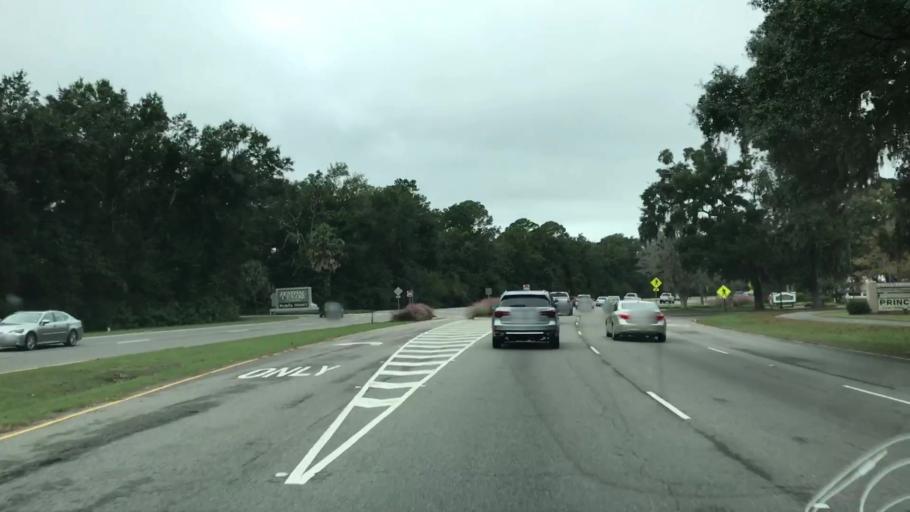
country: US
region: South Carolina
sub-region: Beaufort County
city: Hilton Head Island
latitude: 32.2127
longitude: -80.7250
